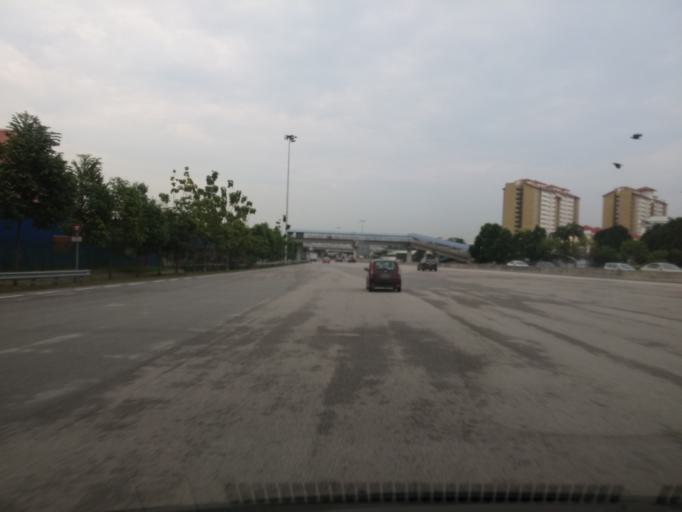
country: MY
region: Kuala Lumpur
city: Kuala Lumpur
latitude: 3.1117
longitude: 101.7125
